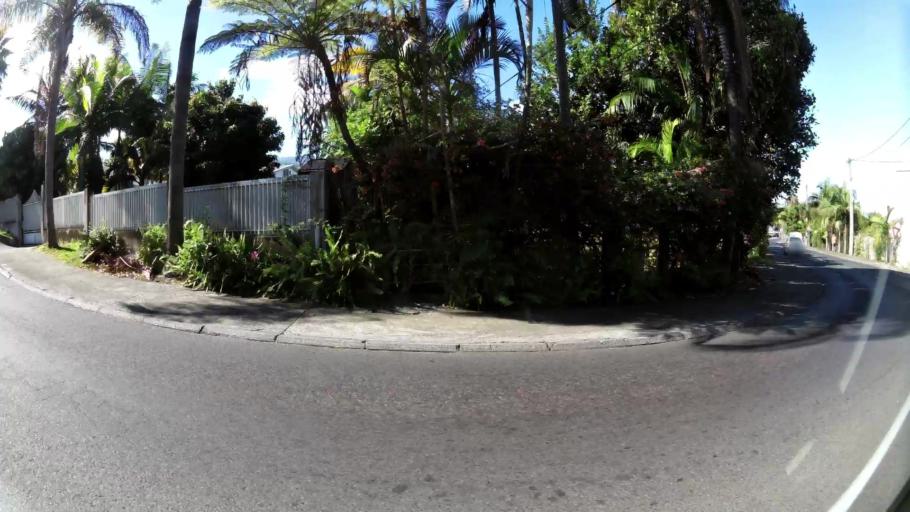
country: RE
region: Reunion
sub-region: Reunion
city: Le Tampon
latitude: -21.2774
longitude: 55.5246
